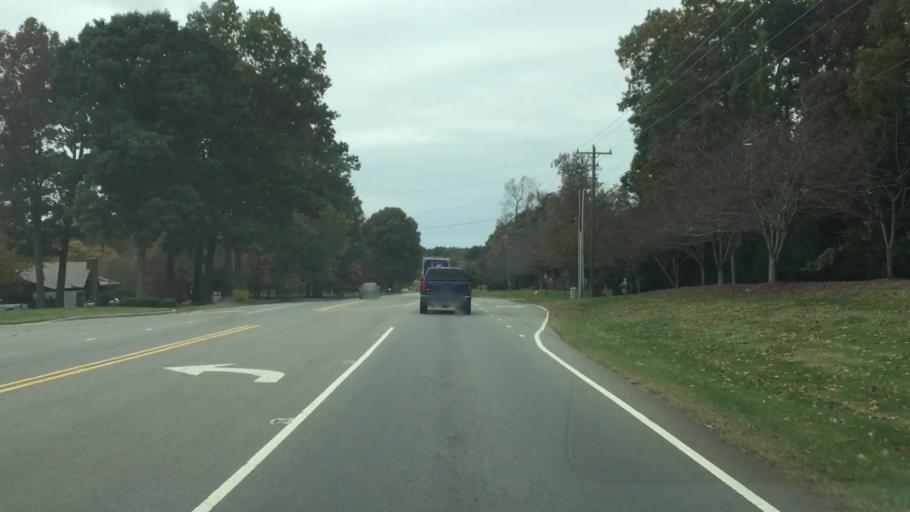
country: US
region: North Carolina
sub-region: Iredell County
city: Mooresville
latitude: 35.6046
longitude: -80.7787
